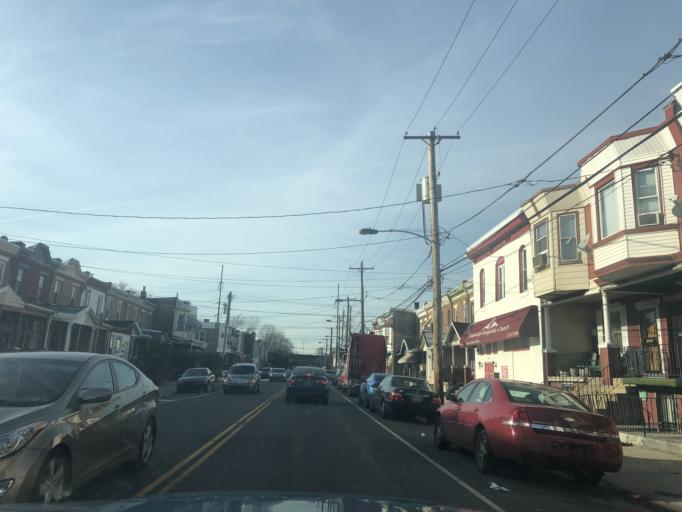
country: US
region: Pennsylvania
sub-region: Montgomery County
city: Bala-Cynwyd
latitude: 39.9796
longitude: -75.2258
